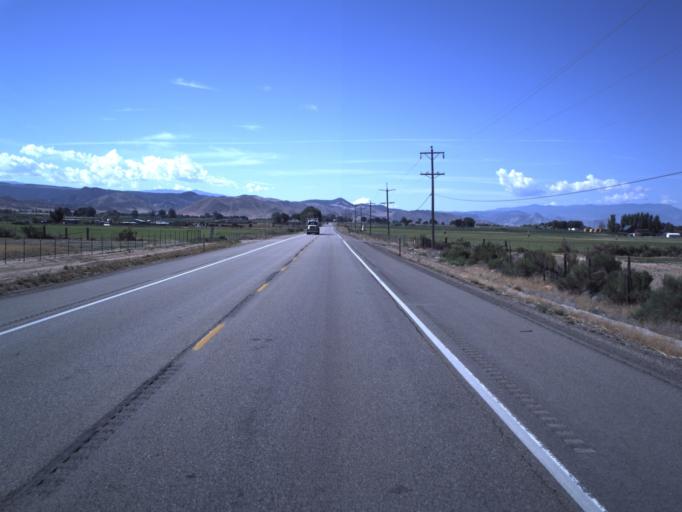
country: US
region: Utah
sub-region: Sanpete County
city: Centerfield
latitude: 39.0782
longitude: -111.8210
